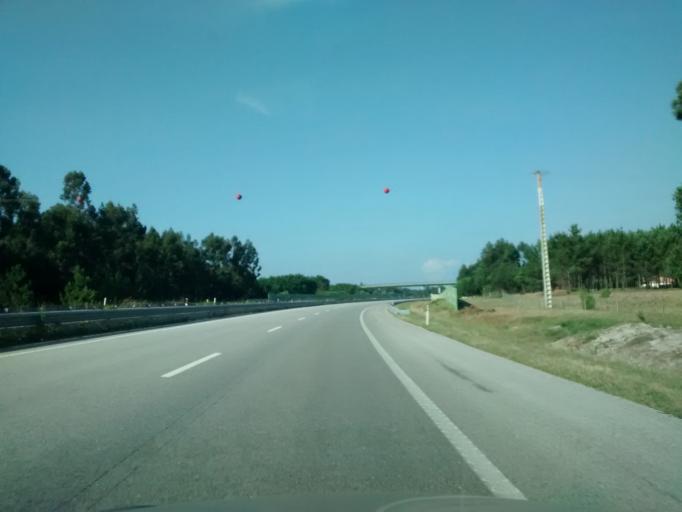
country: PT
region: Coimbra
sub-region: Figueira da Foz
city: Alhadas
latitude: 40.2481
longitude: -8.7798
